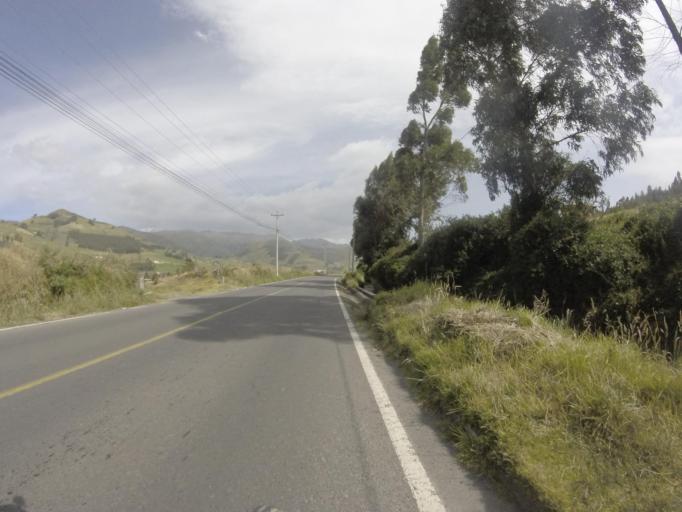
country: EC
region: Pichincha
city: Cayambe
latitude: 0.1218
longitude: -78.0858
